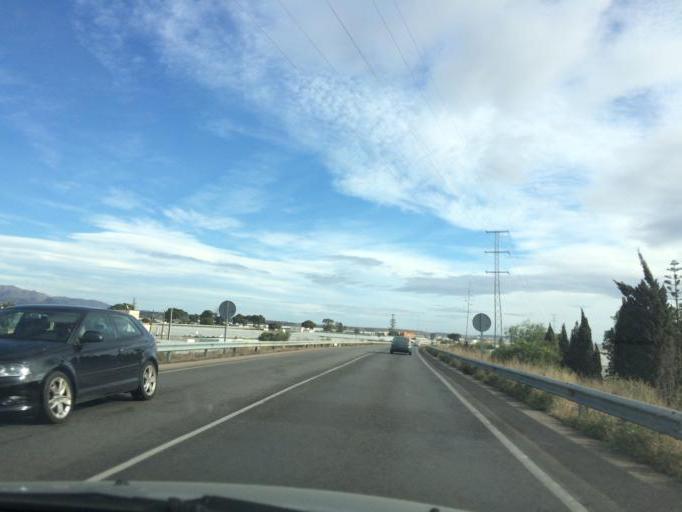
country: ES
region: Andalusia
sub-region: Provincia de Almeria
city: Retamar
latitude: 36.8561
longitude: -2.3643
